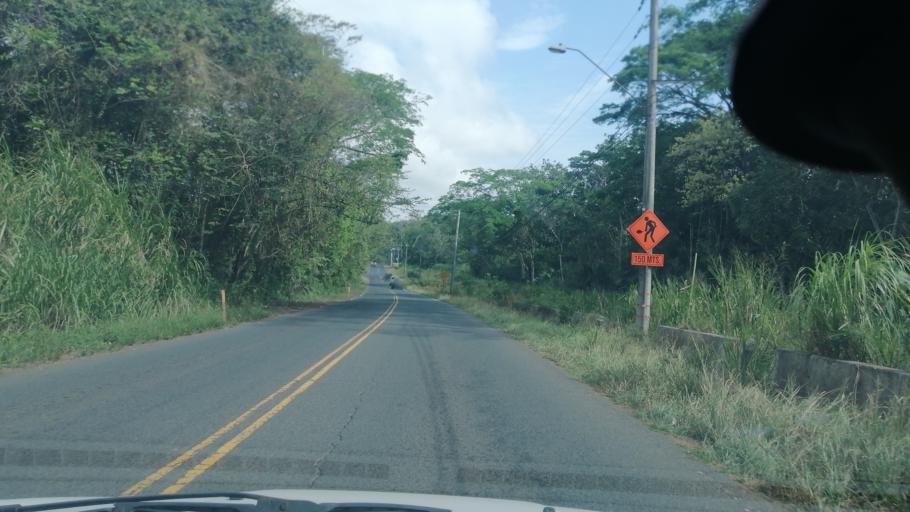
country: PA
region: Panama
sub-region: Distrito de Panama
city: Paraiso
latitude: 9.0442
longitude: -79.6352
